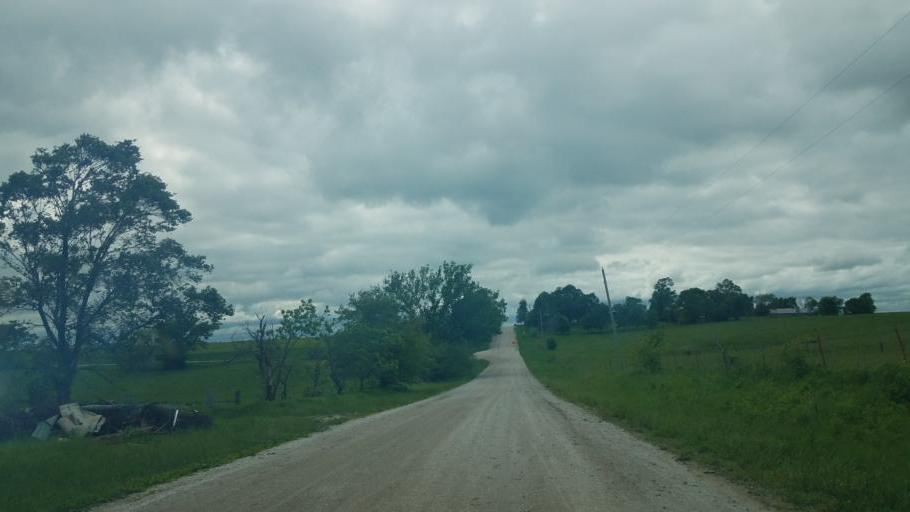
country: US
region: Iowa
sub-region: Decatur County
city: Lamoni
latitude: 40.5948
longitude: -93.8514
